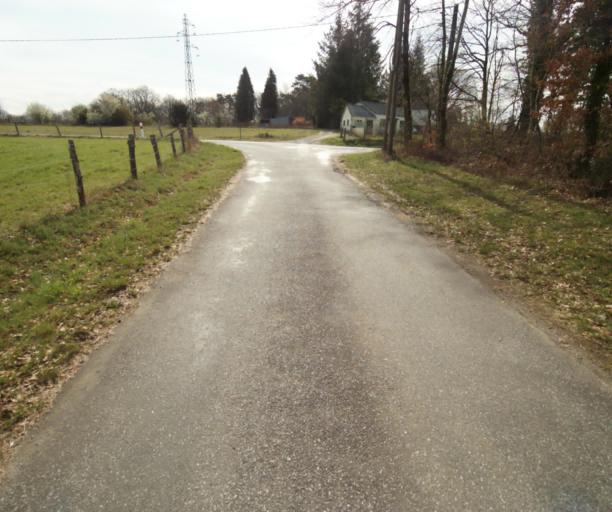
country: FR
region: Limousin
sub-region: Departement de la Correze
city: Correze
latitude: 45.3325
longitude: 1.8700
